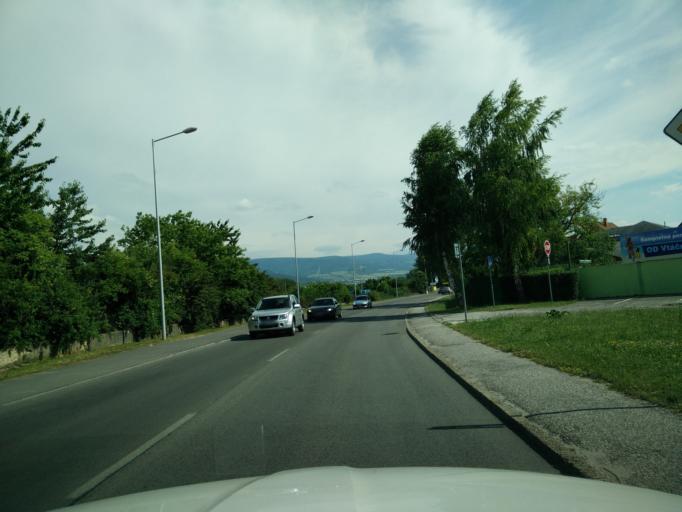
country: SK
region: Nitriansky
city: Bojnice
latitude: 48.7824
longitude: 18.5911
